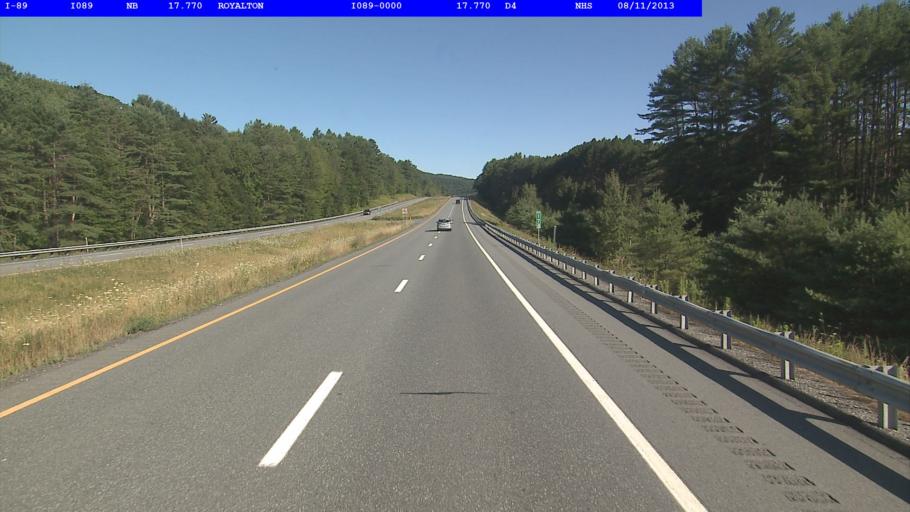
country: US
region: Vermont
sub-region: Orange County
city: Randolph
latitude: 43.8111
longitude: -72.5201
